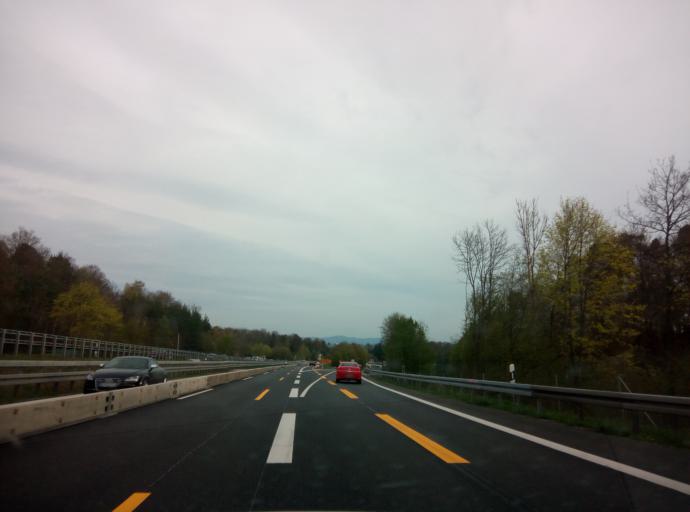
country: DE
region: Baden-Wuerttemberg
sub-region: Tuebingen Region
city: Sickenhausen
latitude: 48.5586
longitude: 9.1732
